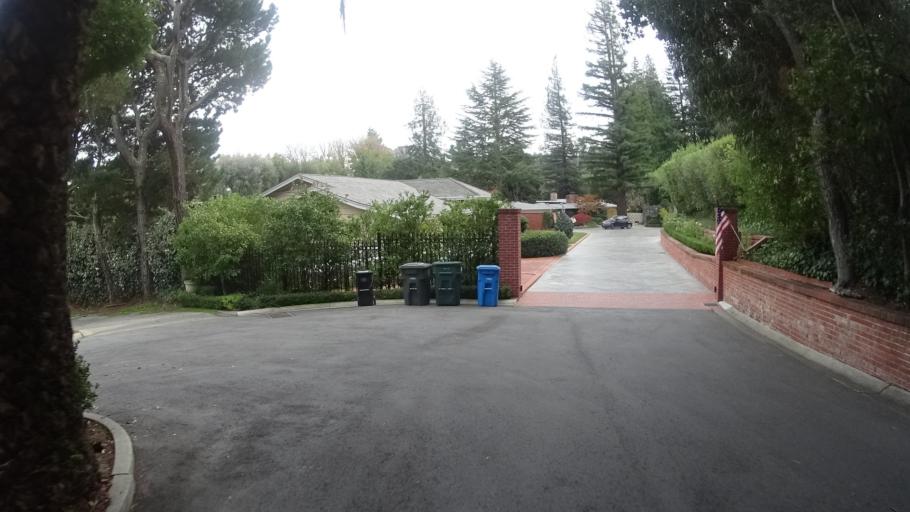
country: US
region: California
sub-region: San Mateo County
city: Burlingame
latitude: 37.5753
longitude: -122.3698
